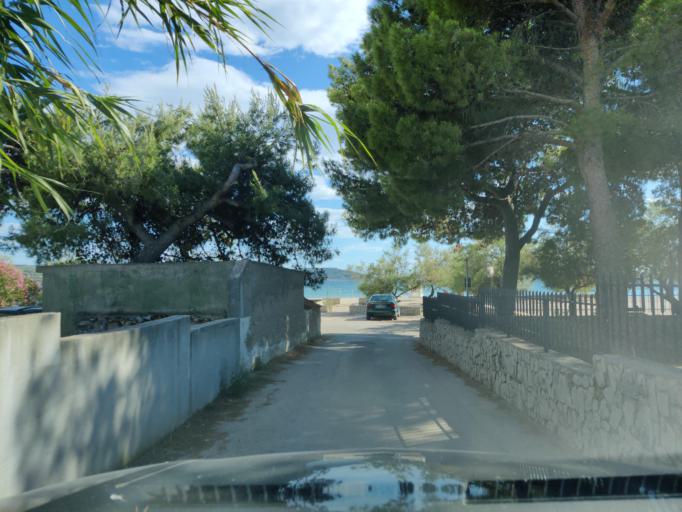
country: HR
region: Sibensko-Kniniska
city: Zaton
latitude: 43.7276
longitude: 15.8382
